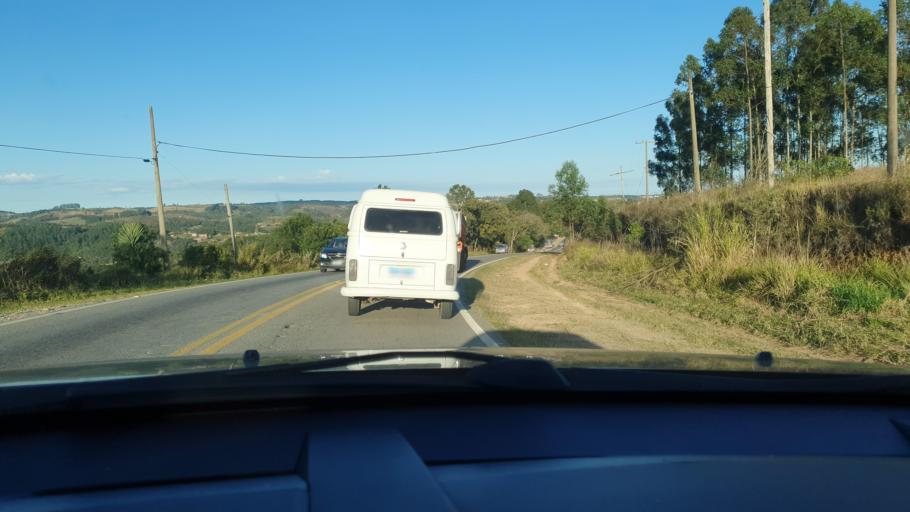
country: BR
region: Sao Paulo
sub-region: Piedade
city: Piedade
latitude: -23.7145
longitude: -47.3752
